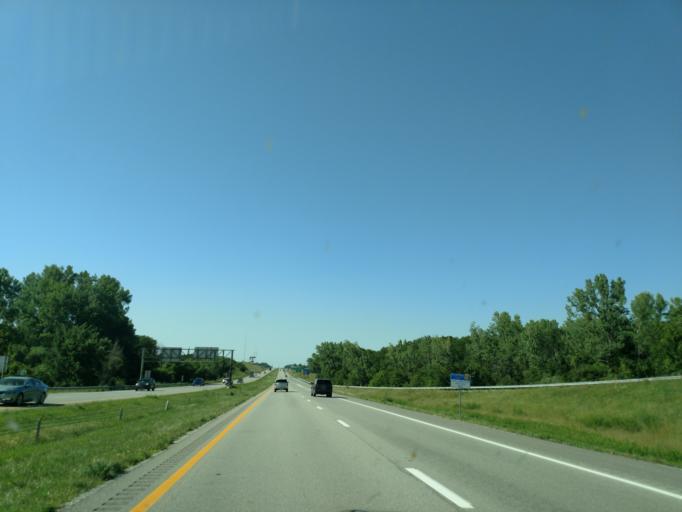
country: US
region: Missouri
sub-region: Buchanan County
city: Saint Joseph
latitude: 39.7097
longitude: -94.7884
